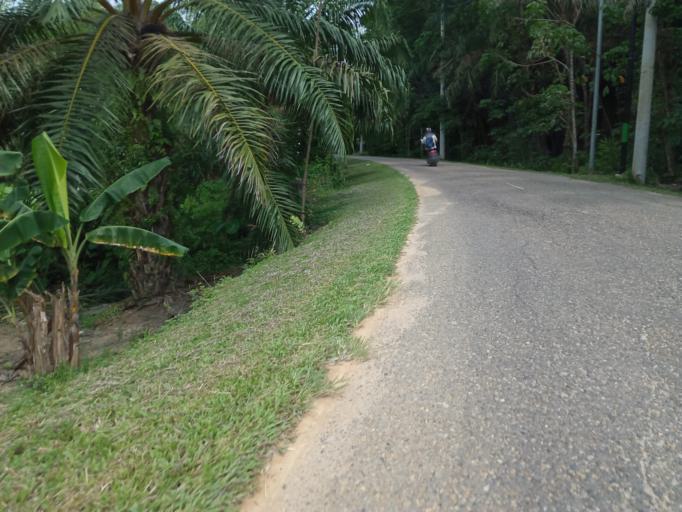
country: ID
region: Jambi
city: Muara Bulian
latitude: -1.7096
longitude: 103.2597
